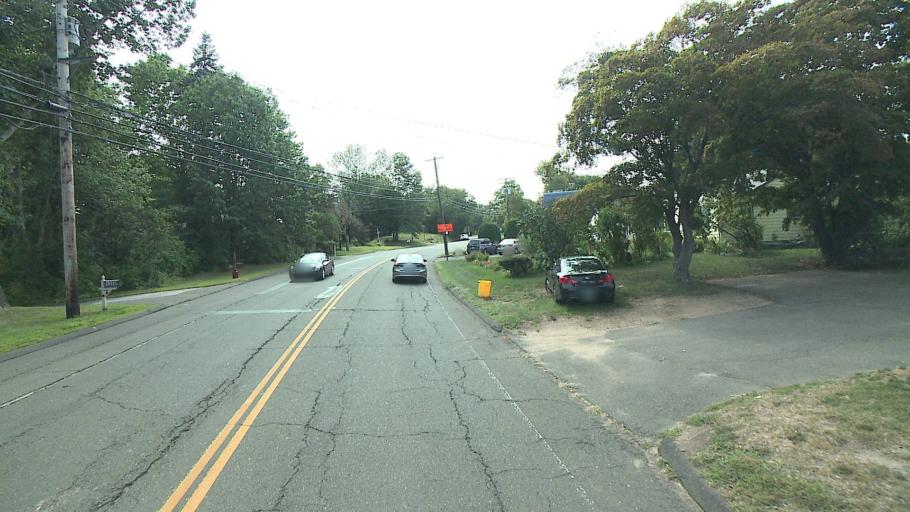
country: US
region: Connecticut
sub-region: Fairfield County
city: Stratford
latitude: 41.2236
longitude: -73.1154
